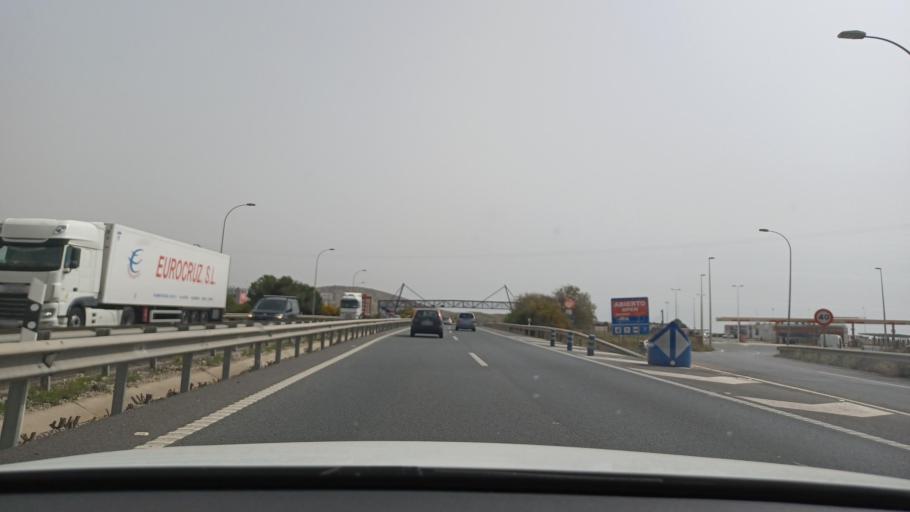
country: ES
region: Valencia
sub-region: Provincia de Alicante
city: Elche
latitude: 38.3085
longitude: -0.6089
